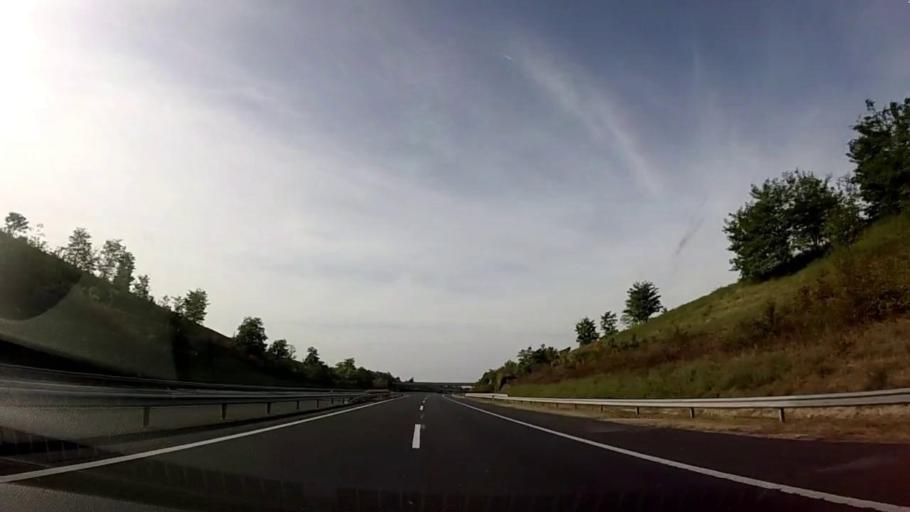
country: HU
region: Somogy
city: Balatonszarszo
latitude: 46.8146
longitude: 17.8494
